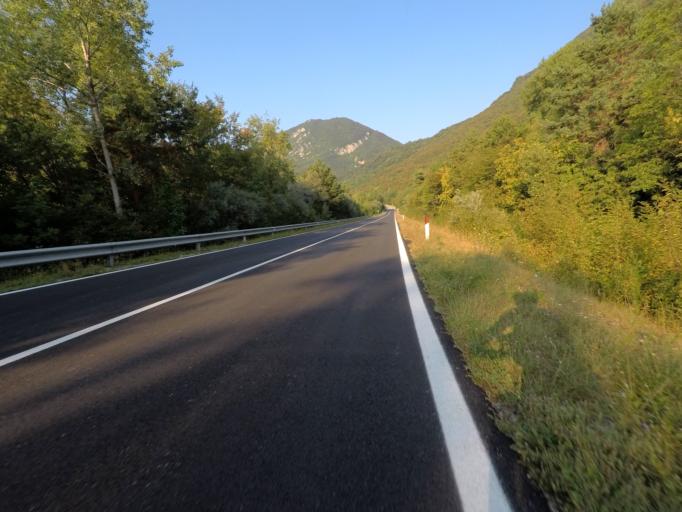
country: IT
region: Friuli Venezia Giulia
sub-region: Provincia di Udine
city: Trasaghis
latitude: 46.2682
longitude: 13.0527
